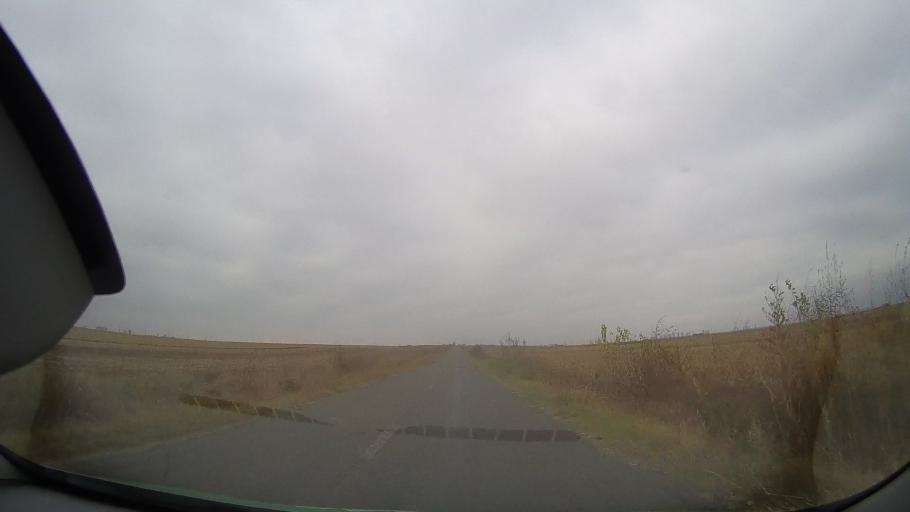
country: RO
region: Buzau
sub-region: Comuna Luciu
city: Luciu
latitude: 44.9766
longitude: 27.0587
